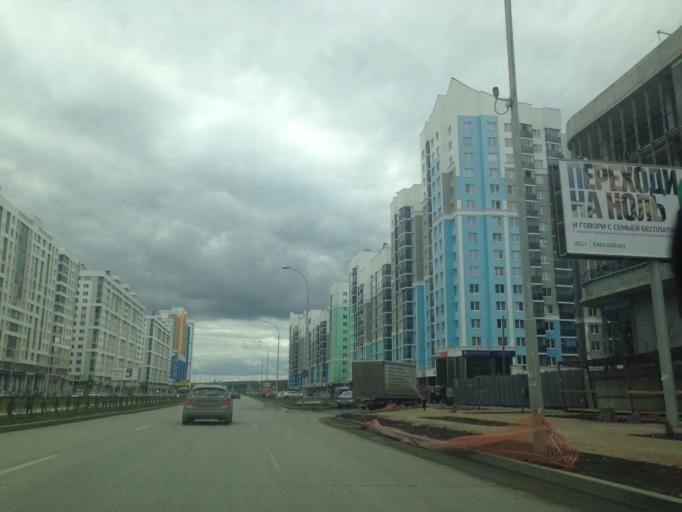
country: RU
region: Sverdlovsk
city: Shirokaya Rechka
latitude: 56.7928
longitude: 60.5208
